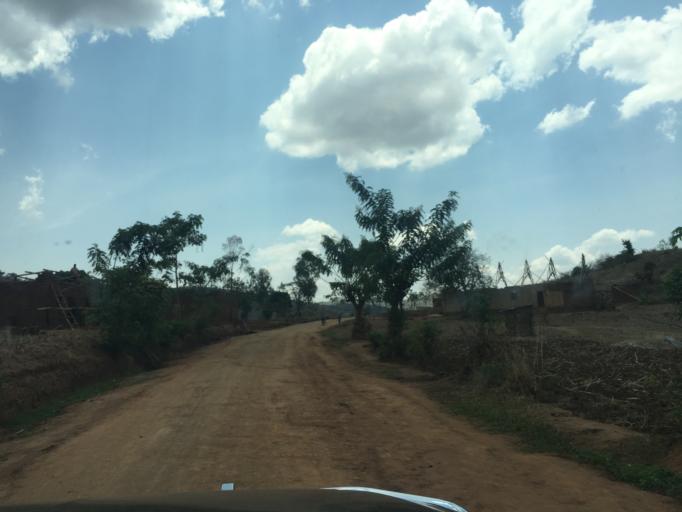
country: RW
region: Eastern Province
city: Kibungo
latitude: -2.1167
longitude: 30.8490
